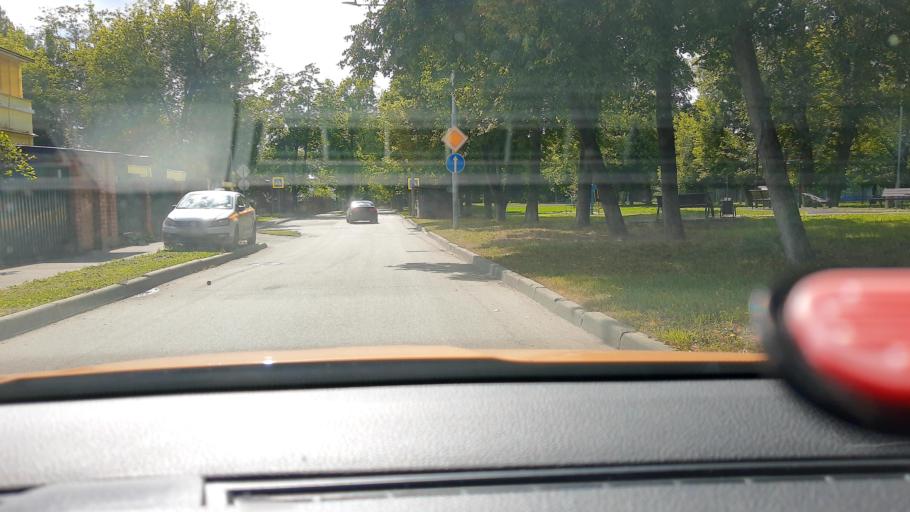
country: RU
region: Moskovskaya
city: Kur'yanovo
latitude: 55.6558
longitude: 37.6988
